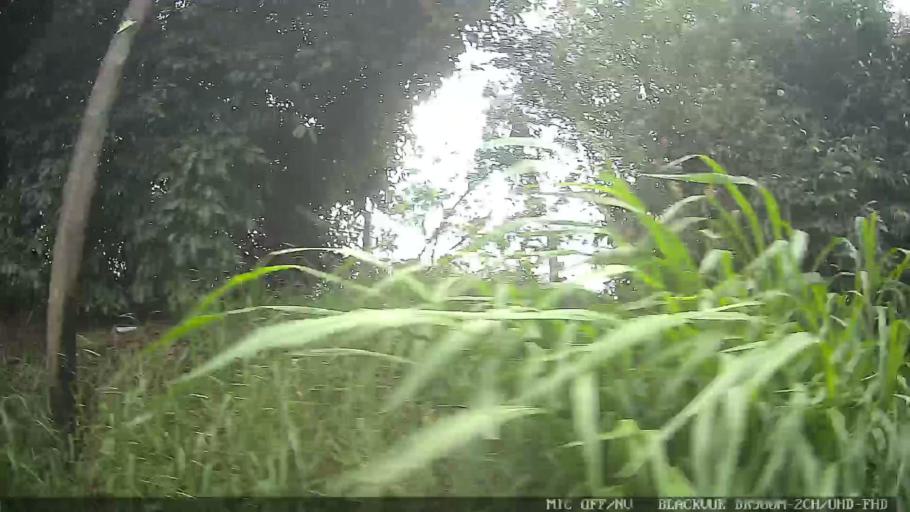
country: BR
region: Sao Paulo
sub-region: Atibaia
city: Atibaia
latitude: -23.0975
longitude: -46.6377
